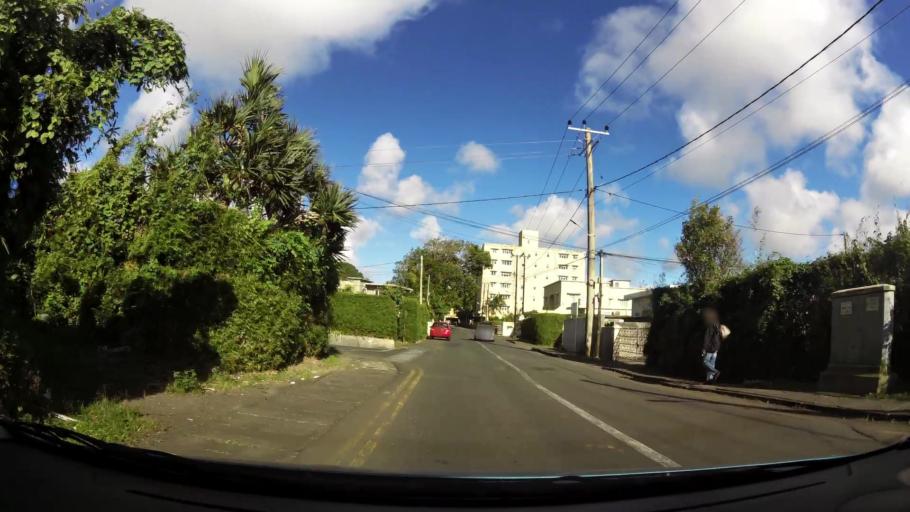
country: MU
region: Plaines Wilhems
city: Curepipe
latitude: -20.3182
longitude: 57.5304
